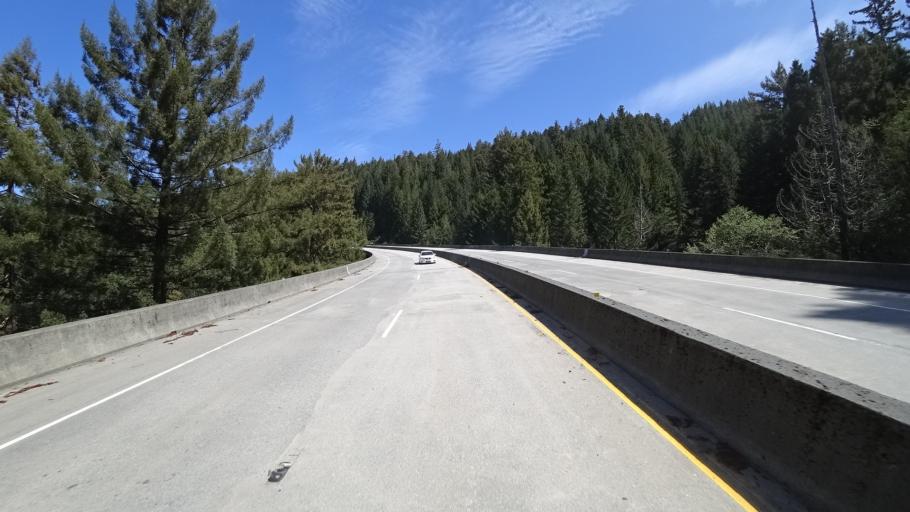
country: US
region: California
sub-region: Humboldt County
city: Westhaven-Moonstone
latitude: 41.3701
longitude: -123.9909
